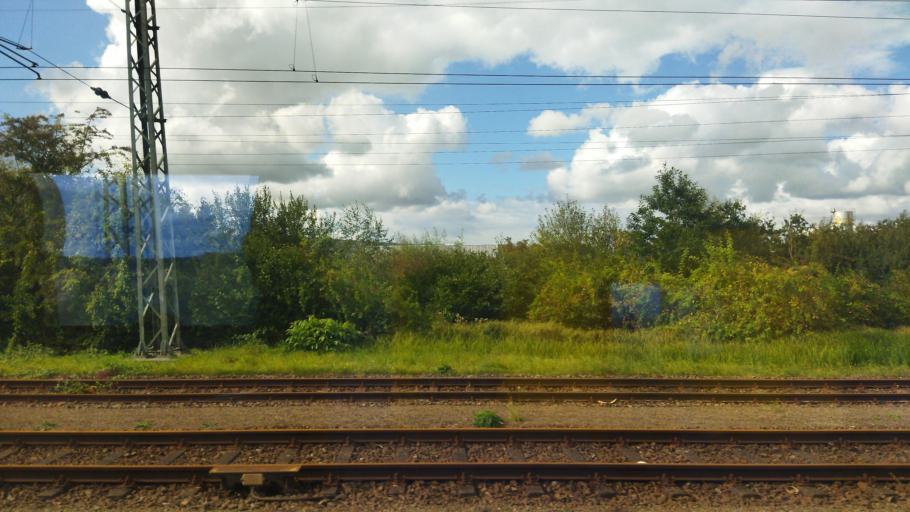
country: DE
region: Lower Saxony
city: Leer
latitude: 53.2221
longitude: 7.4650
